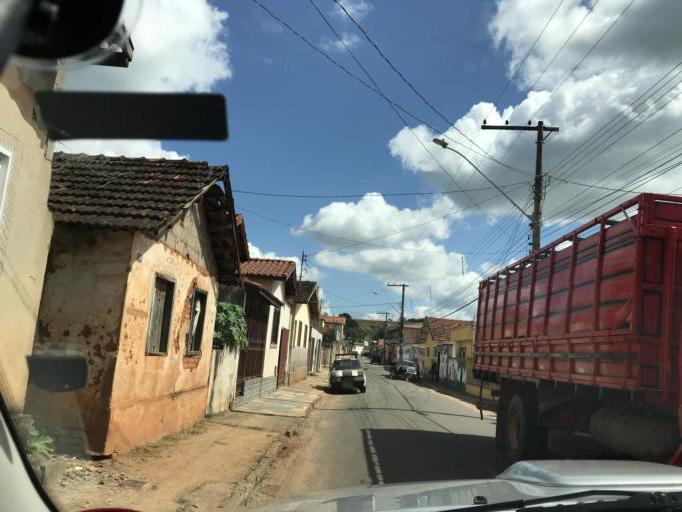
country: BR
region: Minas Gerais
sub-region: Campanha
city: Campanha
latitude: -21.8322
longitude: -45.4072
